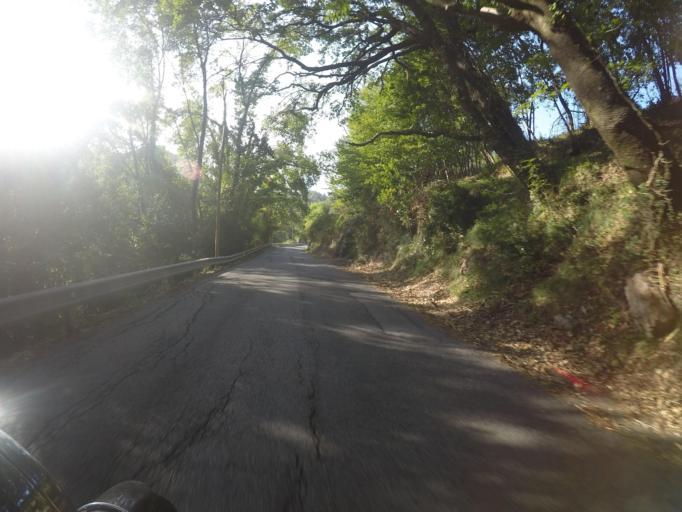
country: IT
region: Tuscany
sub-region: Provincia di Massa-Carrara
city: Carrara
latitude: 44.0838
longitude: 10.0913
